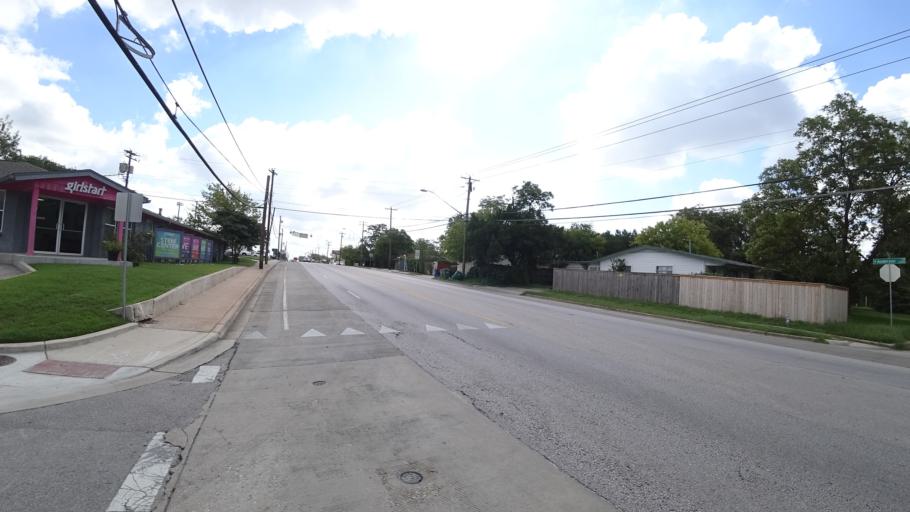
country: US
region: Texas
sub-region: Travis County
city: Austin
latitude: 30.3511
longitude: -97.7201
